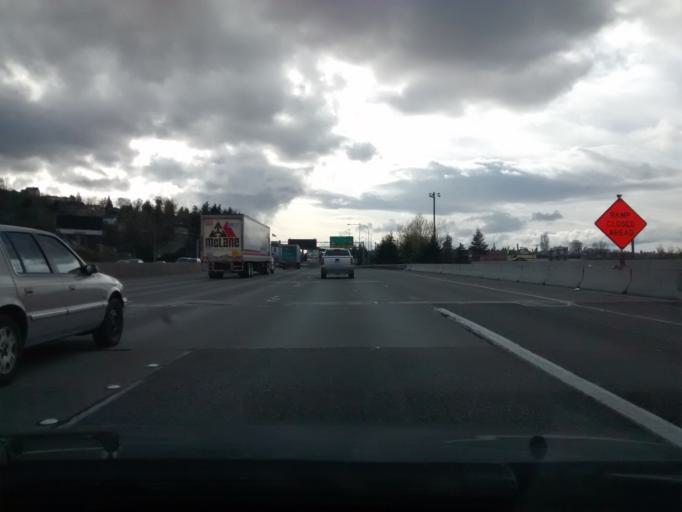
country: US
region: Washington
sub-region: Pierce County
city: Tacoma
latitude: 47.2393
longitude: -122.4097
